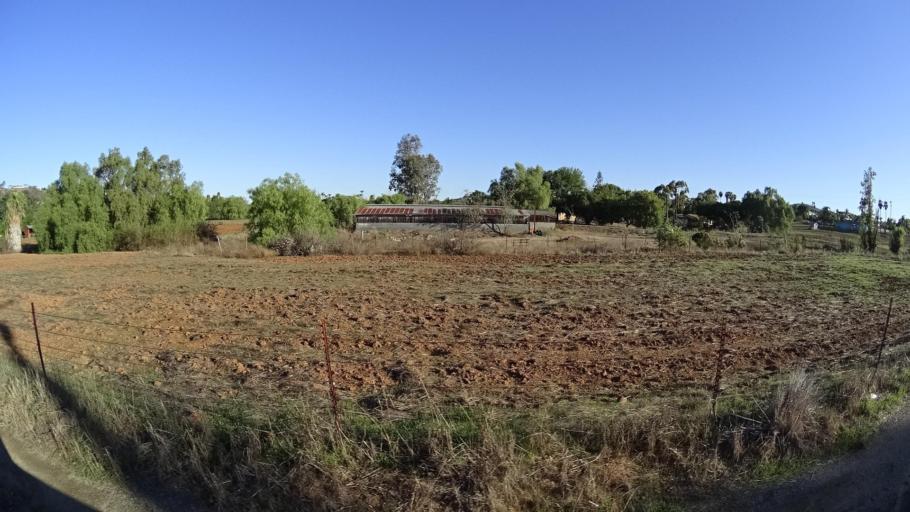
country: US
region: California
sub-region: San Diego County
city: Jamul
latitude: 32.7066
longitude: -116.8834
